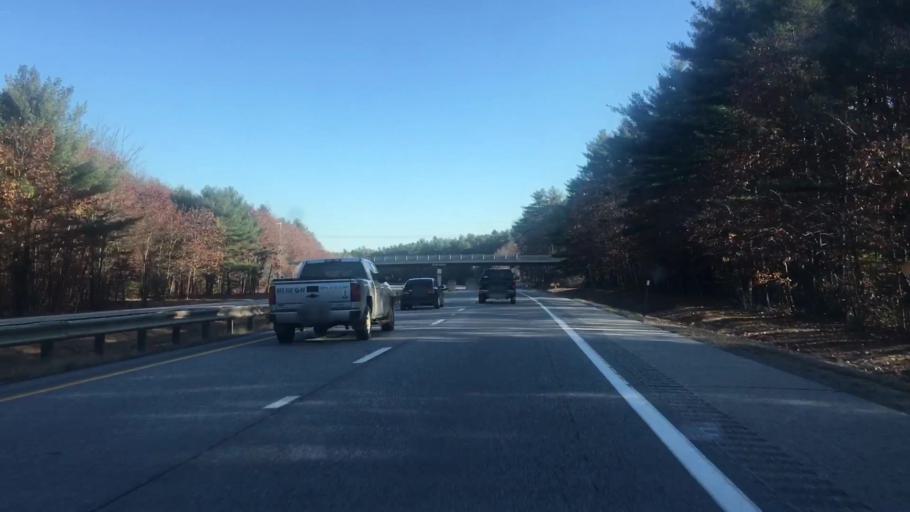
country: US
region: Maine
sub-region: Cumberland County
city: New Gloucester
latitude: 43.9760
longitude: -70.3169
